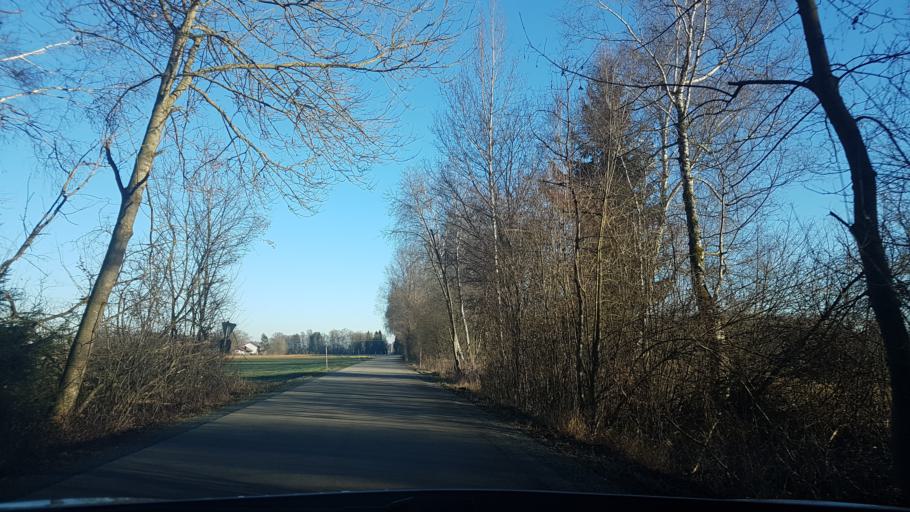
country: DE
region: Bavaria
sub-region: Upper Bavaria
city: Eichenried
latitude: 48.2807
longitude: 11.7713
